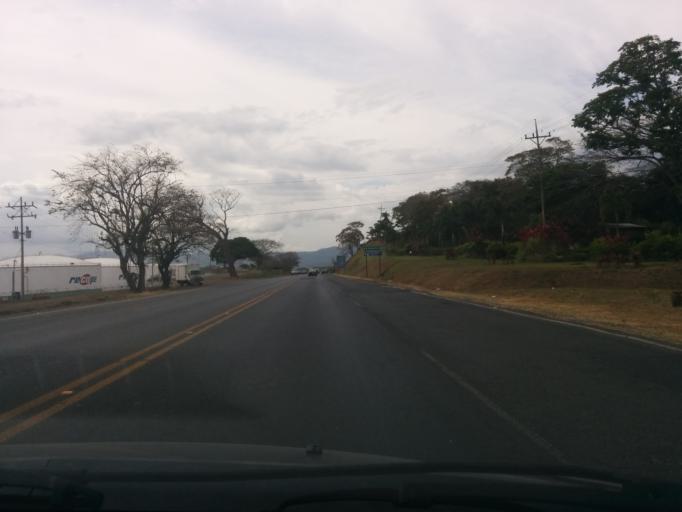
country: CR
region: Alajuela
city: Carrillos
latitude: 10.0040
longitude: -84.2903
